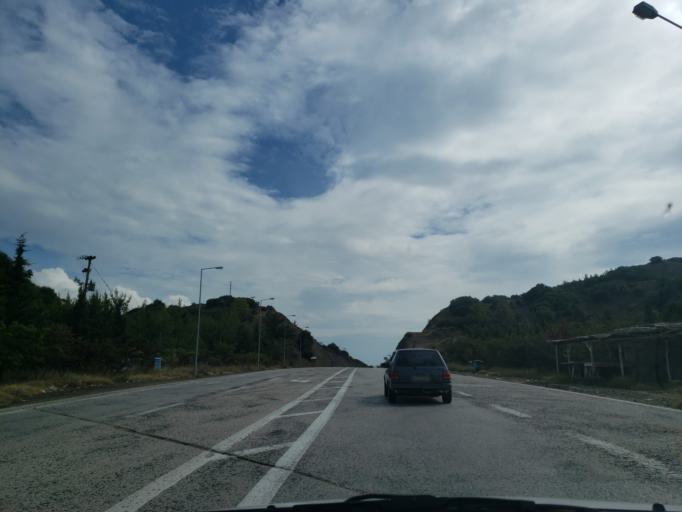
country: GR
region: Central Greece
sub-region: Nomos Fthiotidos
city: Stavros
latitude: 38.9888
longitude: 22.3741
